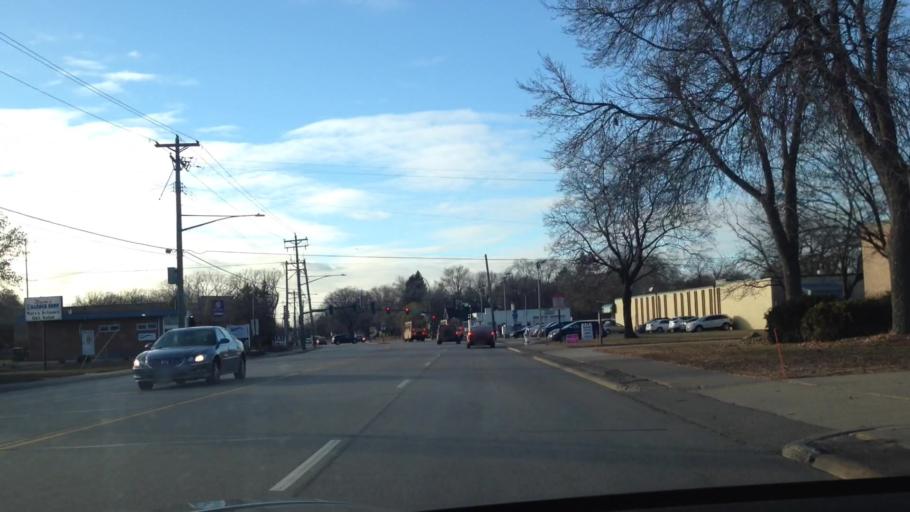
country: US
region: Minnesota
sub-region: Hennepin County
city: Crystal
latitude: 45.0326
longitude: -93.3580
